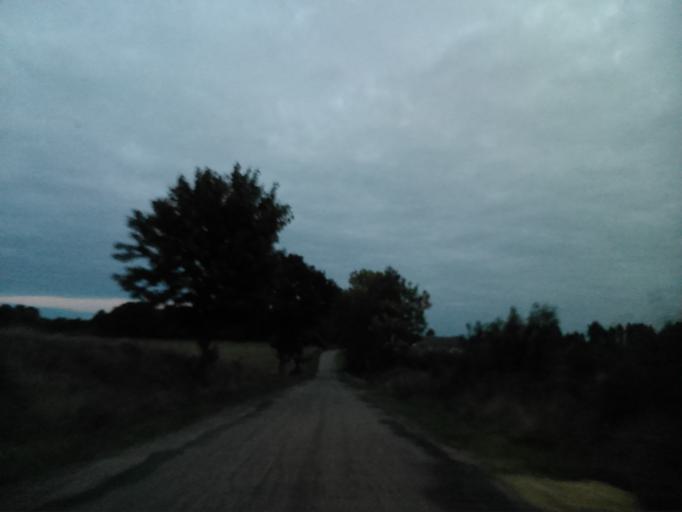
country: PL
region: Kujawsko-Pomorskie
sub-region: Powiat golubsko-dobrzynski
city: Kowalewo Pomorskie
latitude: 53.1270
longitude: 18.9277
